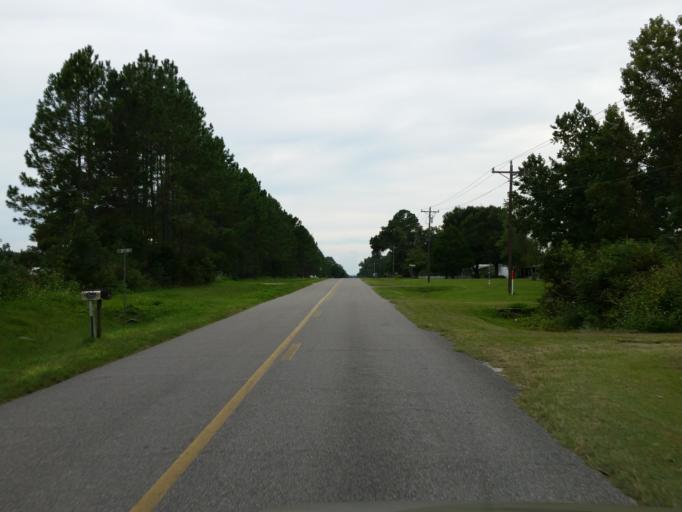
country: US
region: Florida
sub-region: Union County
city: Lake Butler
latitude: 29.9463
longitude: -82.4321
